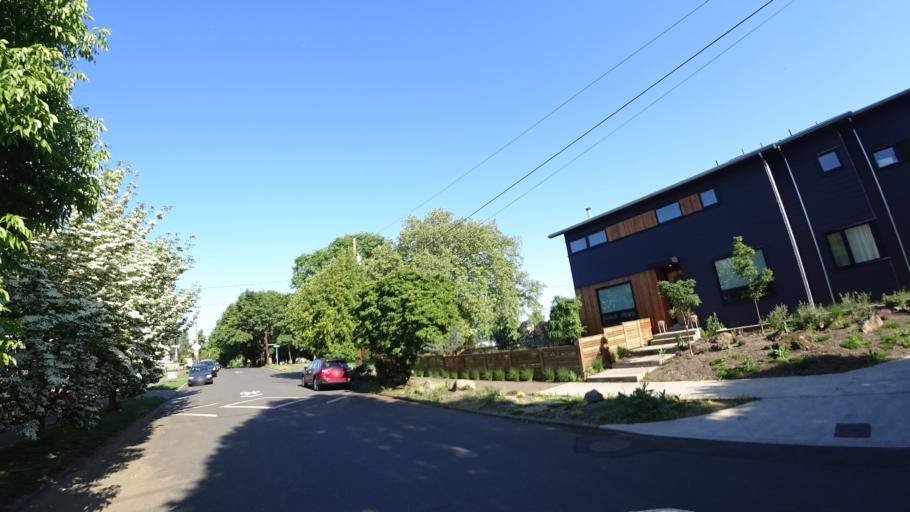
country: US
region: Oregon
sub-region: Multnomah County
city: Portland
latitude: 45.5496
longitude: -122.6839
